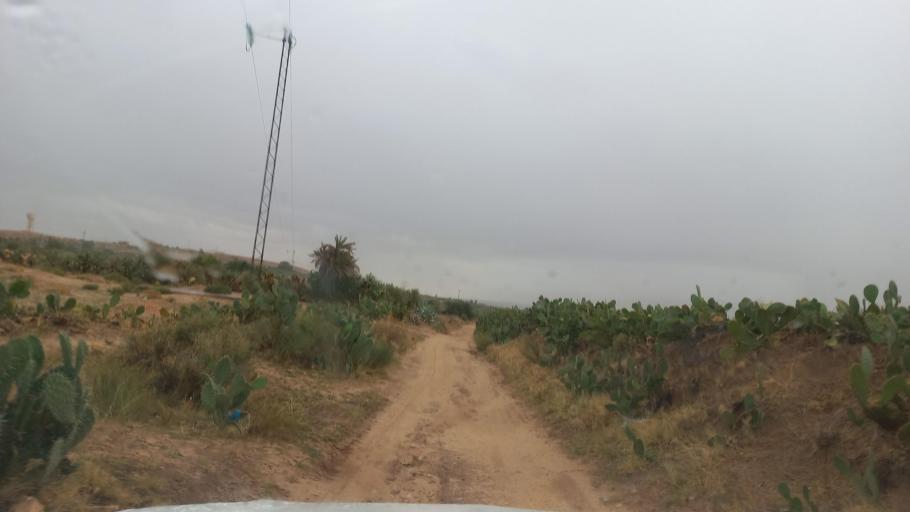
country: TN
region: Al Qasrayn
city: Kasserine
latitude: 35.2737
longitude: 8.9414
